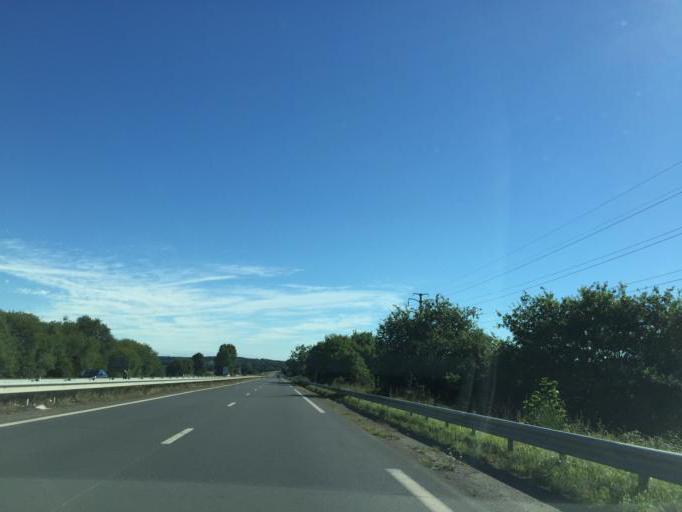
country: FR
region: Brittany
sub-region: Departement des Cotes-d'Armor
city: Quevert
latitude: 48.4606
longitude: -2.0720
